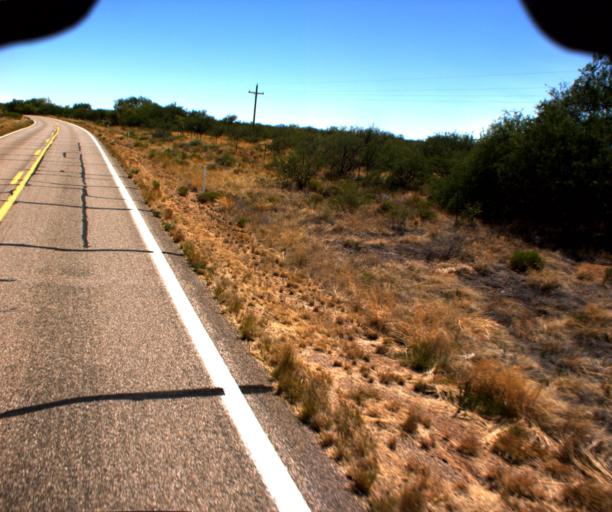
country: US
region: Arizona
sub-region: Pima County
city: Three Points
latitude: 31.7325
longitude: -111.4874
